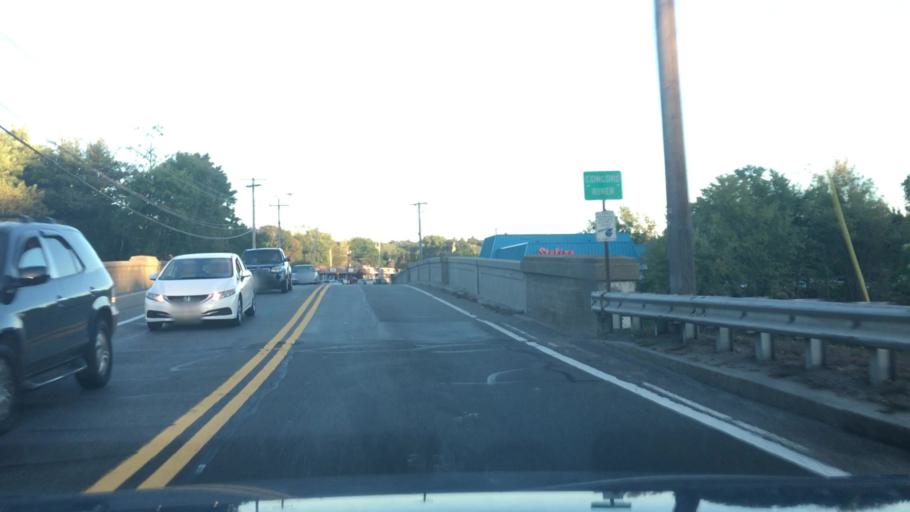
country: US
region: Massachusetts
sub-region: Middlesex County
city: Billerica
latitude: 42.5742
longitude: -71.2807
